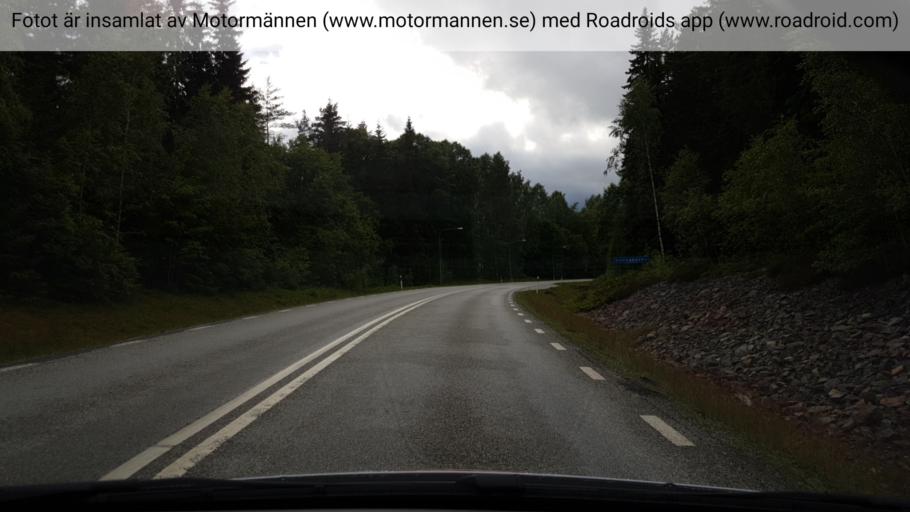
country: SE
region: OErebro
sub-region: Ljusnarsbergs Kommun
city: Kopparberg
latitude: 59.8684
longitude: 15.0267
